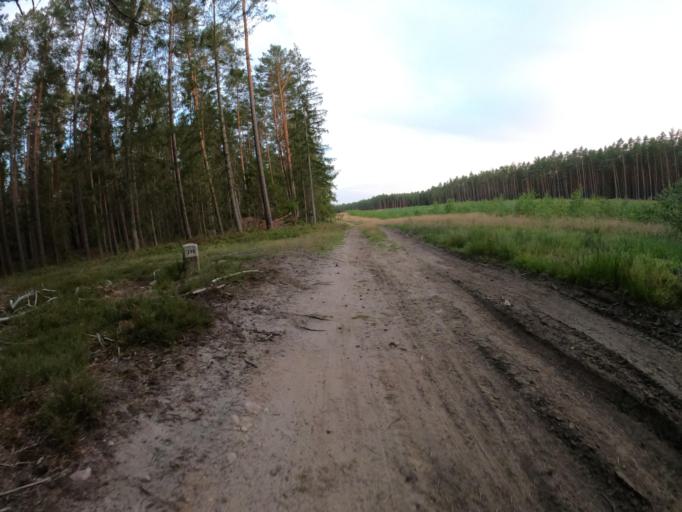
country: PL
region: West Pomeranian Voivodeship
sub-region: Powiat koszalinski
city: Sianow
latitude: 54.1009
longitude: 16.4121
